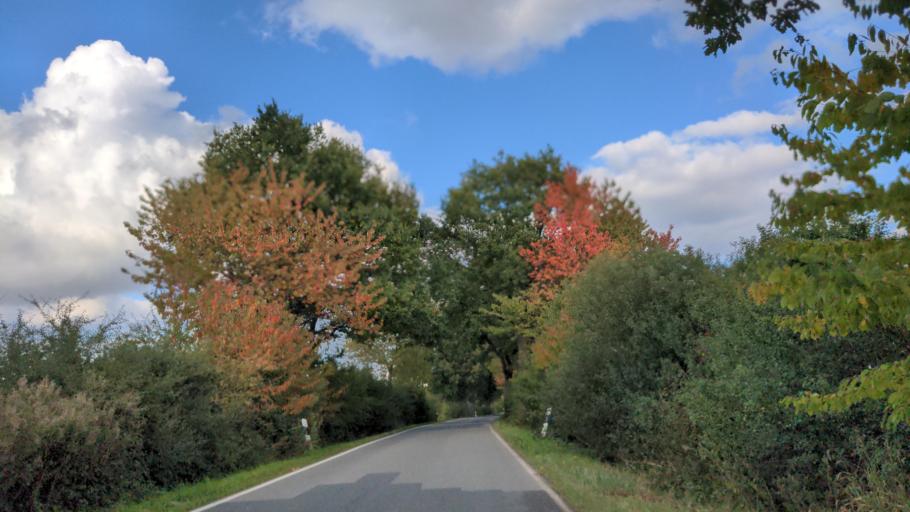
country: DE
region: Schleswig-Holstein
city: Ahrensbok
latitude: 53.9592
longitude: 10.5974
